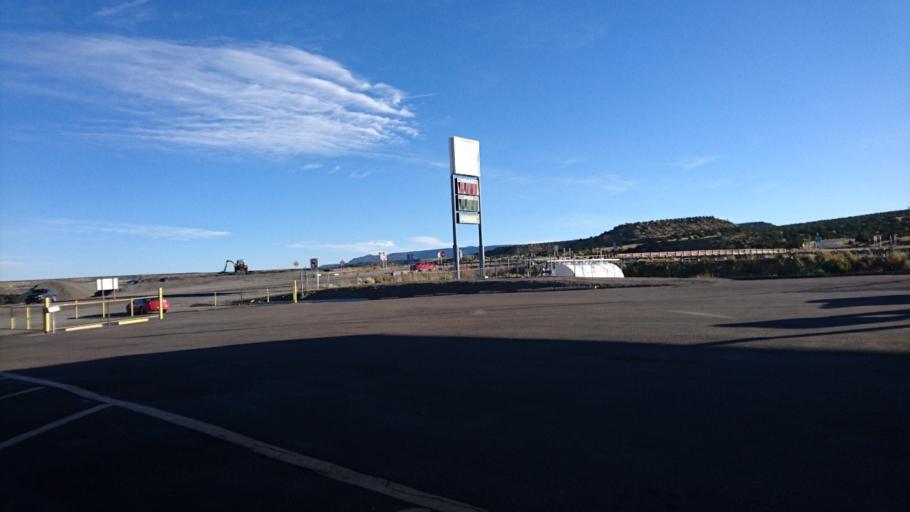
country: US
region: New Mexico
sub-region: Cibola County
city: Grants
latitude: 35.0861
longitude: -107.7699
